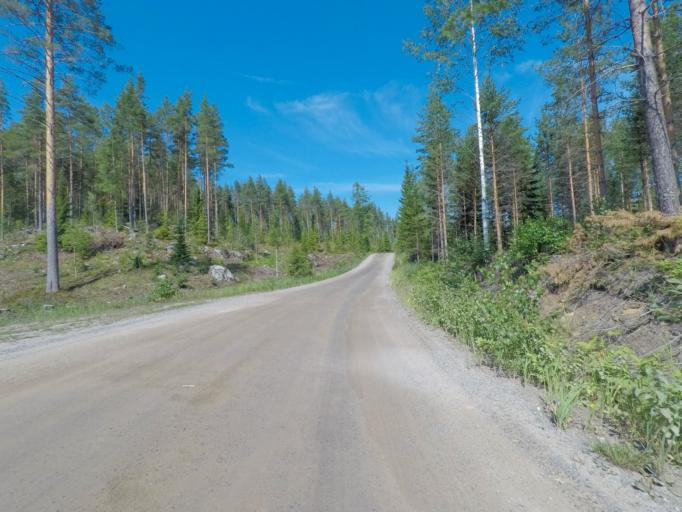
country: FI
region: Southern Savonia
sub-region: Mikkeli
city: Puumala
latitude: 61.4064
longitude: 28.0464
